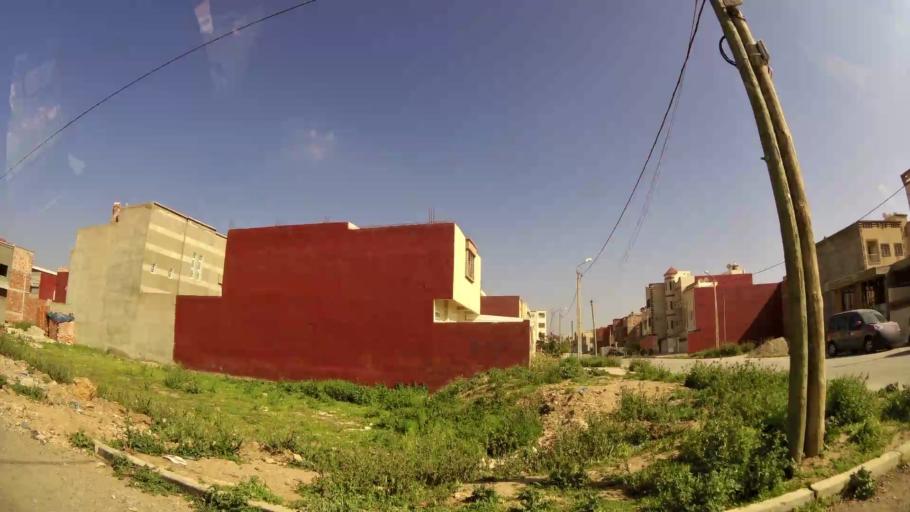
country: MA
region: Oriental
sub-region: Oujda-Angad
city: Oujda
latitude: 34.6983
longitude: -1.8827
